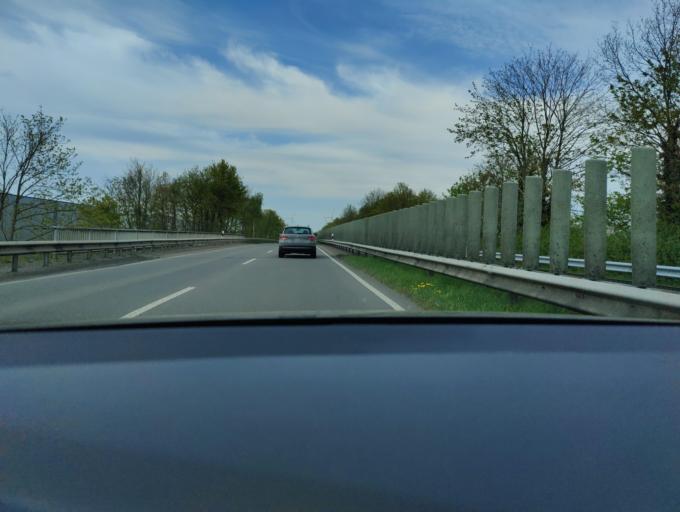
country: NL
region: Overijssel
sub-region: Gemeente Losser
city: Losser
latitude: 52.3094
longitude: 7.0632
